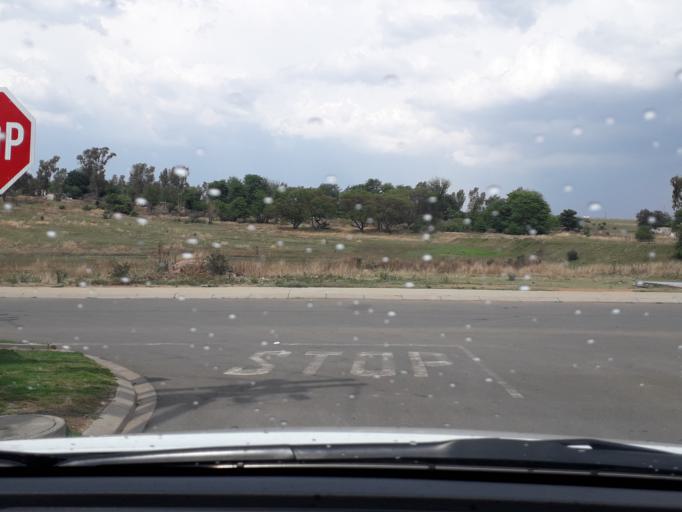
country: ZA
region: Gauteng
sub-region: West Rand District Municipality
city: Muldersdriseloop
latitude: -26.0057
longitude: 27.8530
